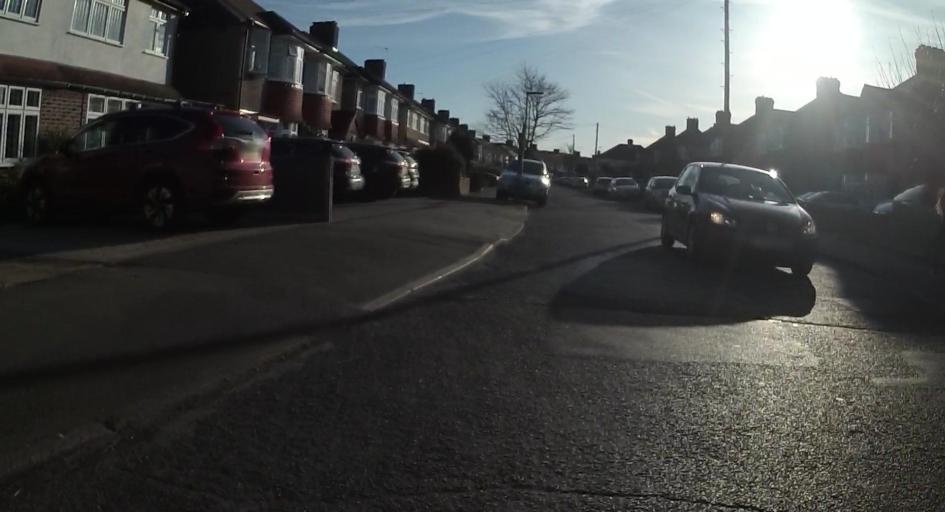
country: GB
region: England
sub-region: Surrey
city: Walton-on-Thames
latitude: 51.3854
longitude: -0.4050
